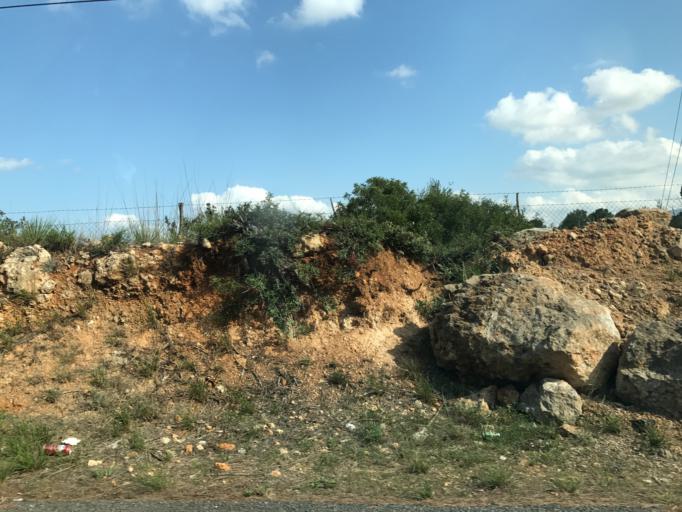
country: ES
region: Balearic Islands
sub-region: Illes Balears
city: Santa Margalida
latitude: 39.7263
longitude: 3.1992
